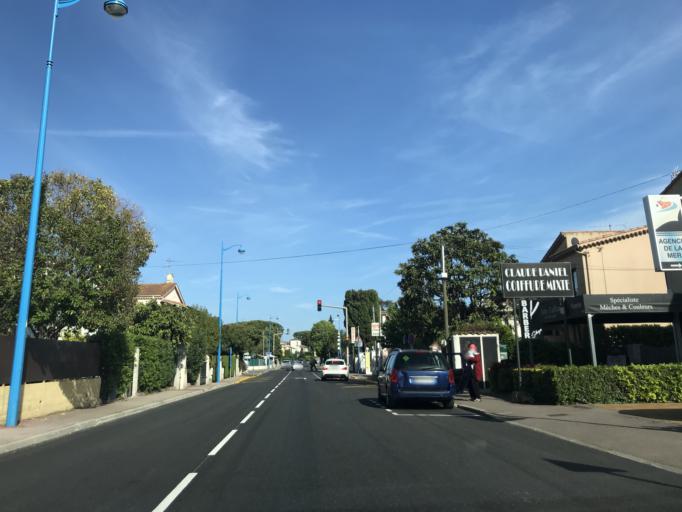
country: FR
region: Provence-Alpes-Cote d'Azur
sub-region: Departement des Alpes-Maritimes
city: Mandelieu-la-Napoule
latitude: 43.5392
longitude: 6.9405
